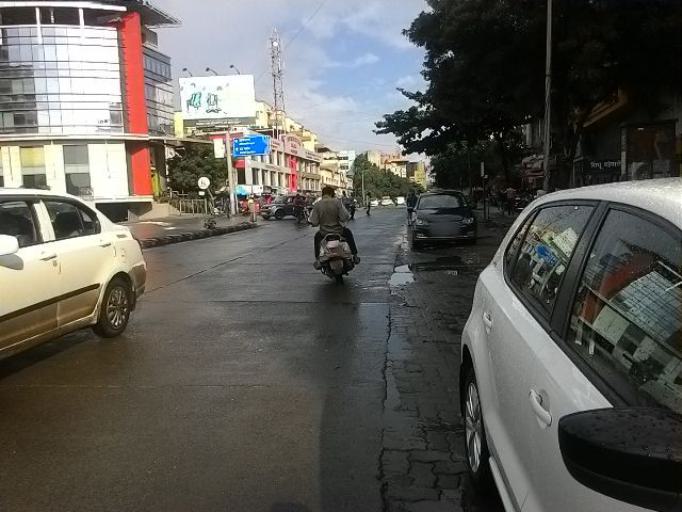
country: IN
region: Maharashtra
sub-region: Pune Division
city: Khadki
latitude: 18.5589
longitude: 73.7914
